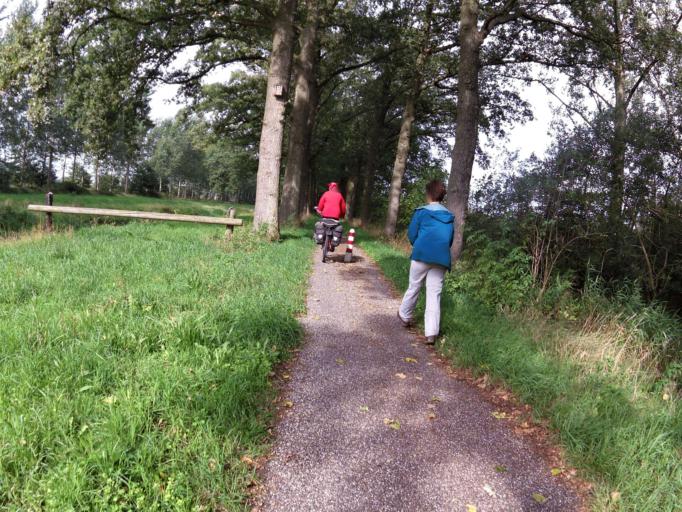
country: NL
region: Gelderland
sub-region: Oude IJsselstreek
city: Varsseveld
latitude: 51.9641
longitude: 6.4296
